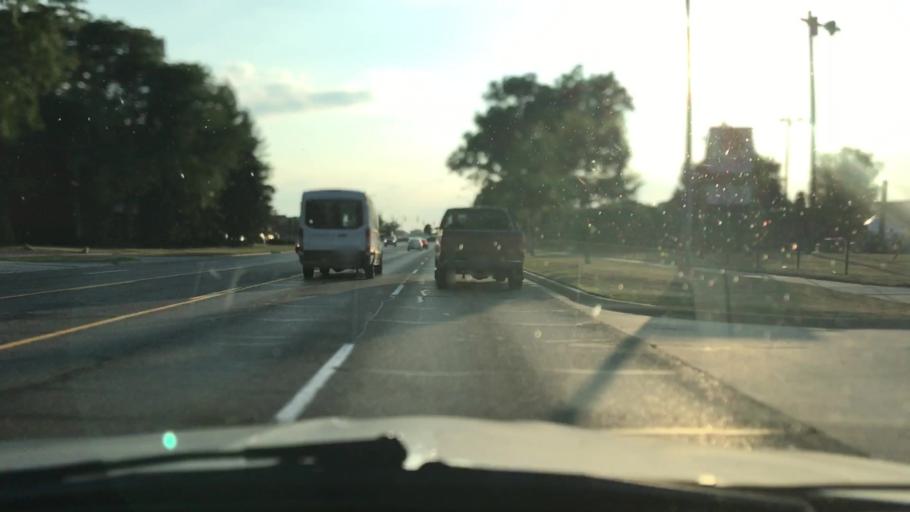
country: US
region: Michigan
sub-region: Oakland County
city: Berkley
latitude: 42.5180
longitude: -83.1809
